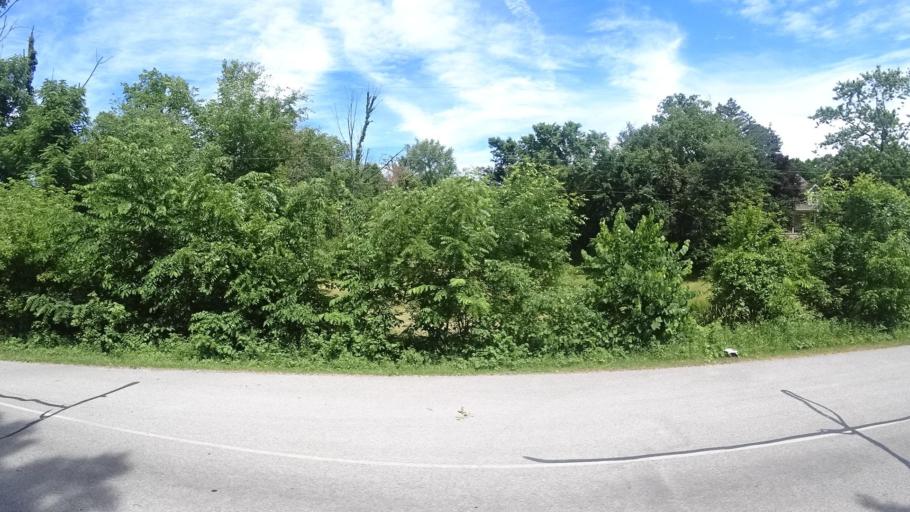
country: US
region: Indiana
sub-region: Porter County
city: Porter
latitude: 41.6239
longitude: -87.0770
